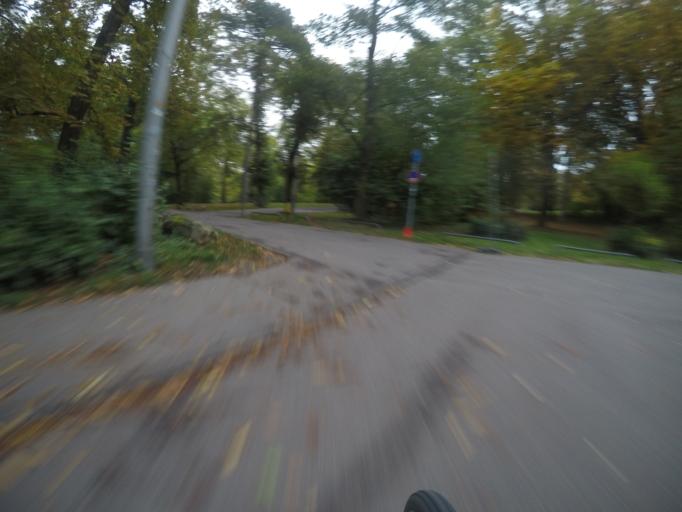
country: DE
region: Baden-Wuerttemberg
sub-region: Regierungsbezirk Stuttgart
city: Stuttgart-Ost
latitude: 48.7943
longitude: 9.2092
